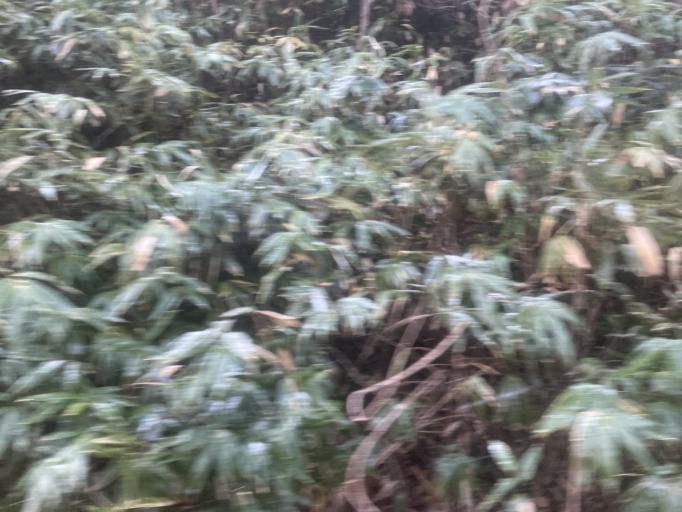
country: JP
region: Aomori
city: Goshogawara
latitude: 41.0804
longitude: 140.5258
